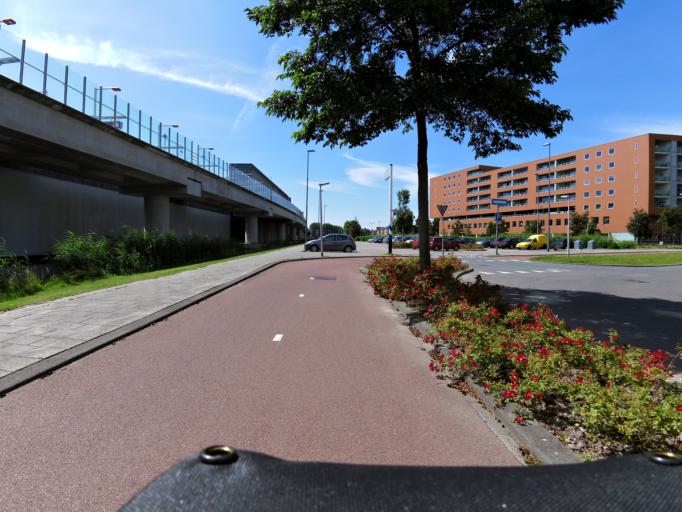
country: NL
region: South Holland
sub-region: Gemeente Albrandswaard
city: Rhoon
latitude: 51.8627
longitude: 4.3780
